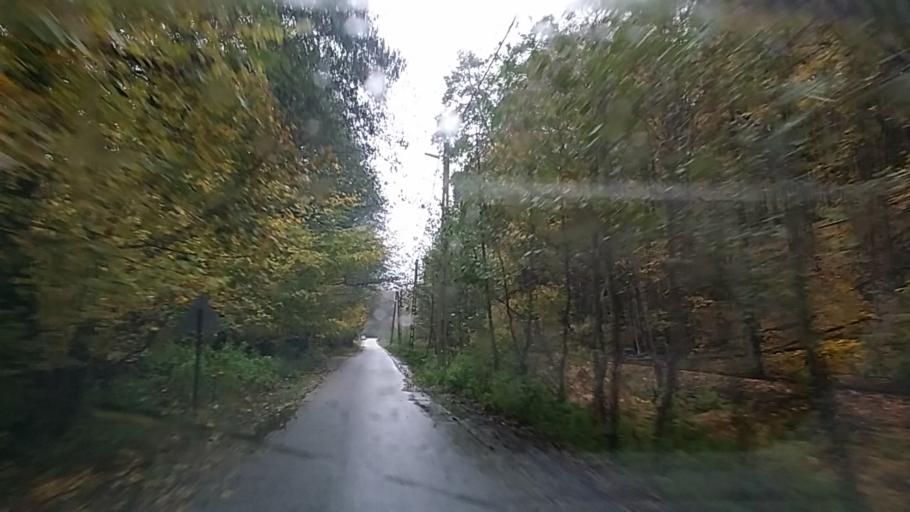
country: HU
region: Borsod-Abauj-Zemplen
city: Tolcsva
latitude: 48.4463
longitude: 21.4619
